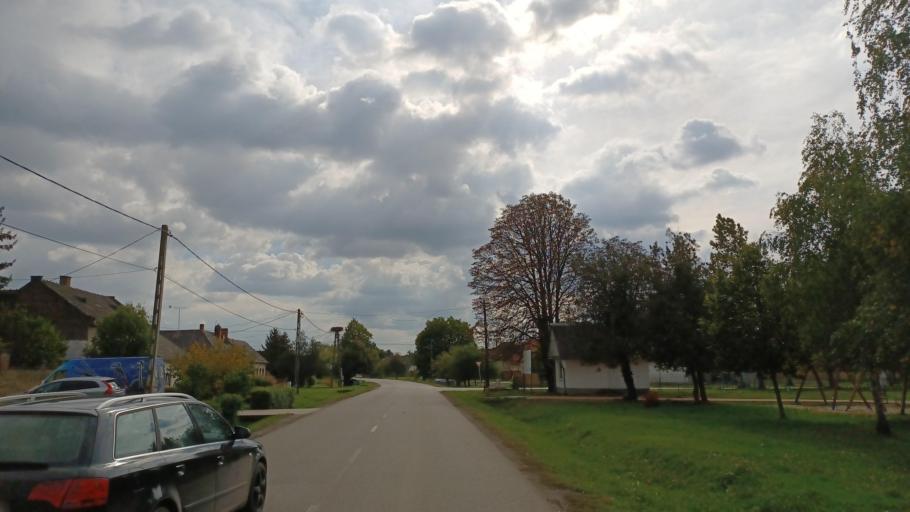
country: HU
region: Tolna
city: Nagydorog
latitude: 46.6236
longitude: 18.6067
